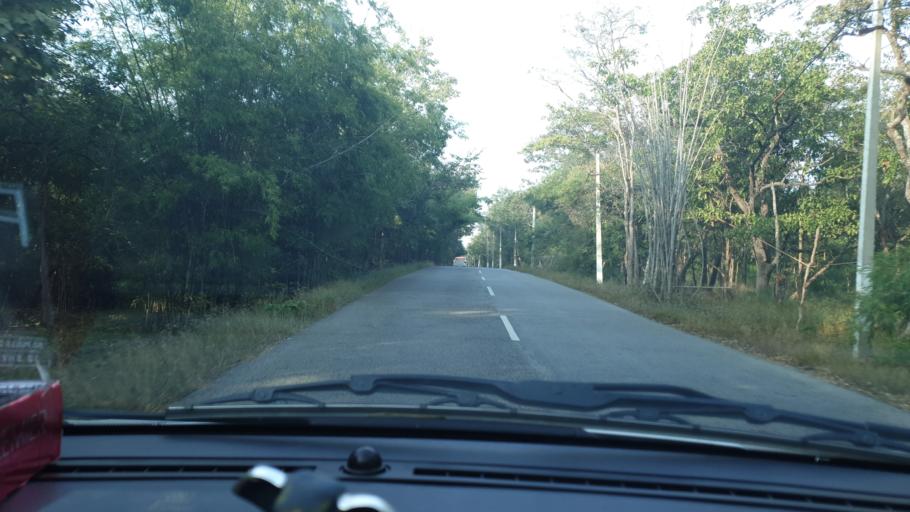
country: IN
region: Andhra Pradesh
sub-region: Kurnool
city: Srisailam
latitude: 16.3001
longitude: 78.7314
